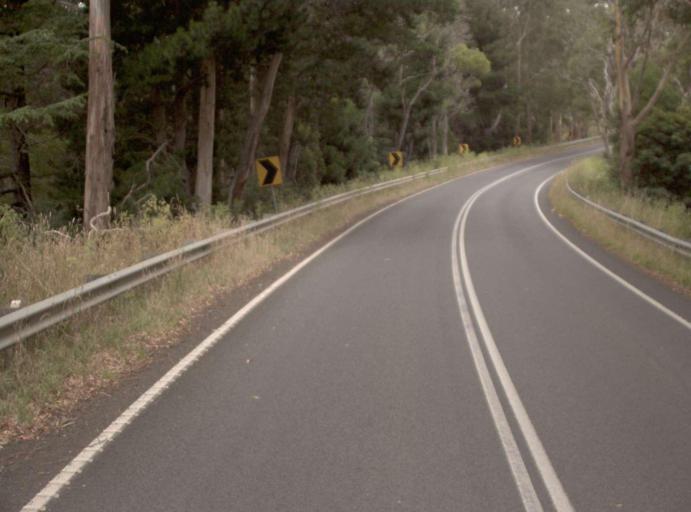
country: AU
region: Victoria
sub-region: Cardinia
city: Bunyip
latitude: -38.1993
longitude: 145.7740
